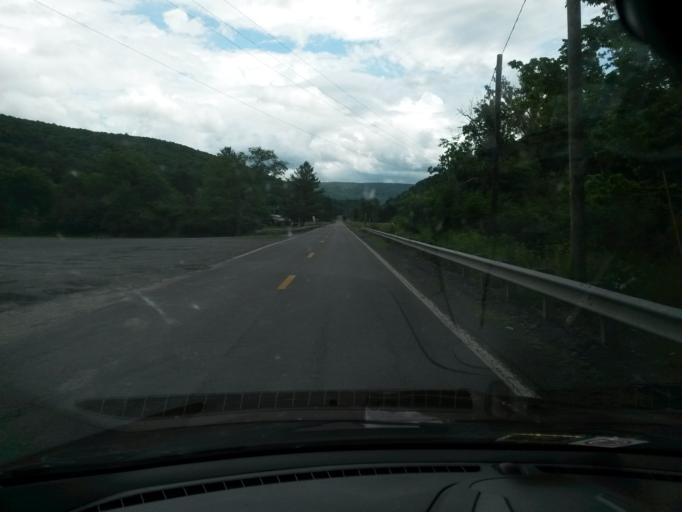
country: US
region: West Virginia
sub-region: Monroe County
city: Union
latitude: 37.5703
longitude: -80.4170
